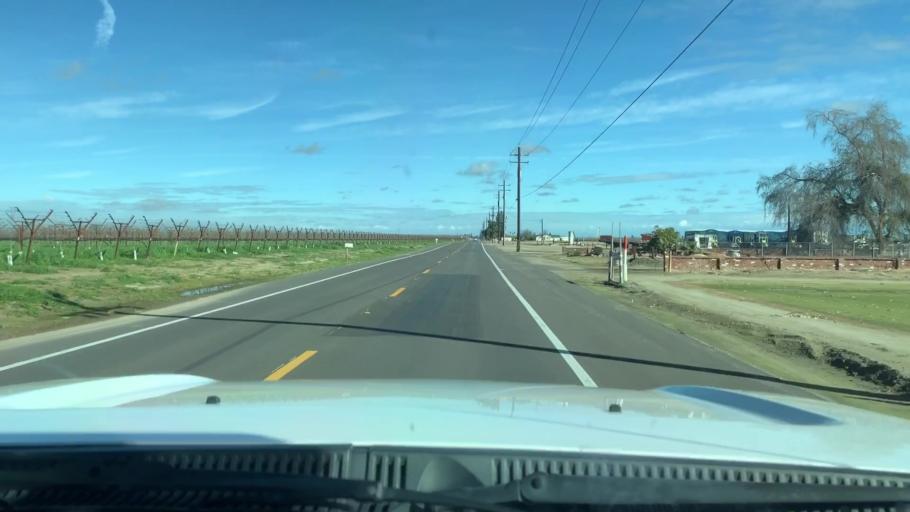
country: US
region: California
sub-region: Fresno County
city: Laton
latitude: 36.5111
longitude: -119.6829
